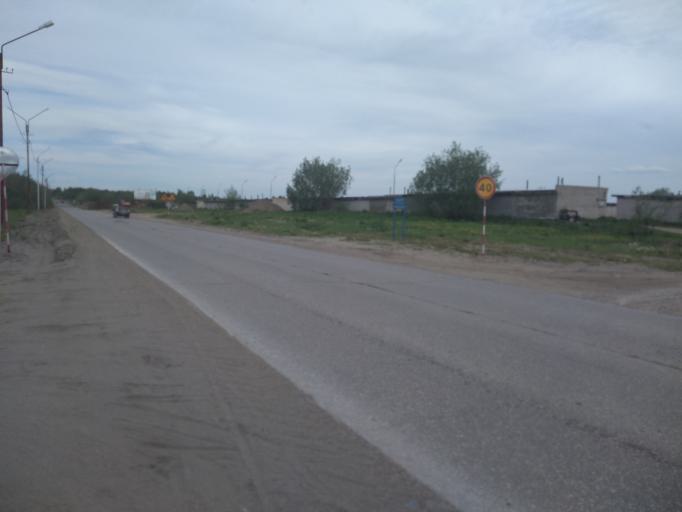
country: RU
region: Komi Republic
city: Pechora
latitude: 65.1429
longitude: 57.2475
